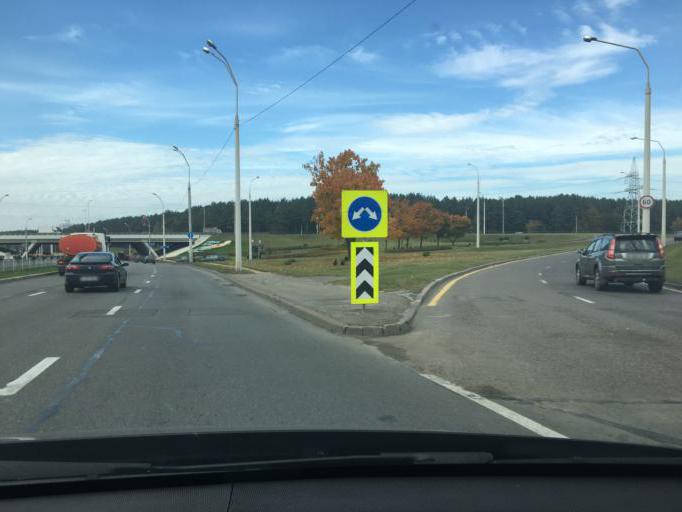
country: BY
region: Minsk
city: Zhdanovichy
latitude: 53.9501
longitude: 27.4481
